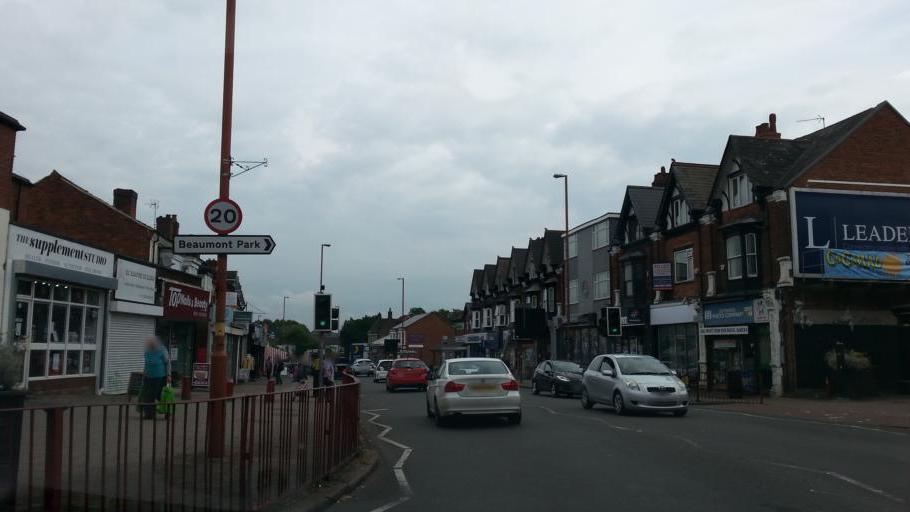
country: GB
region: England
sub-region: City and Borough of Birmingham
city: Bartley Green
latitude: 52.4160
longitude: -1.9303
